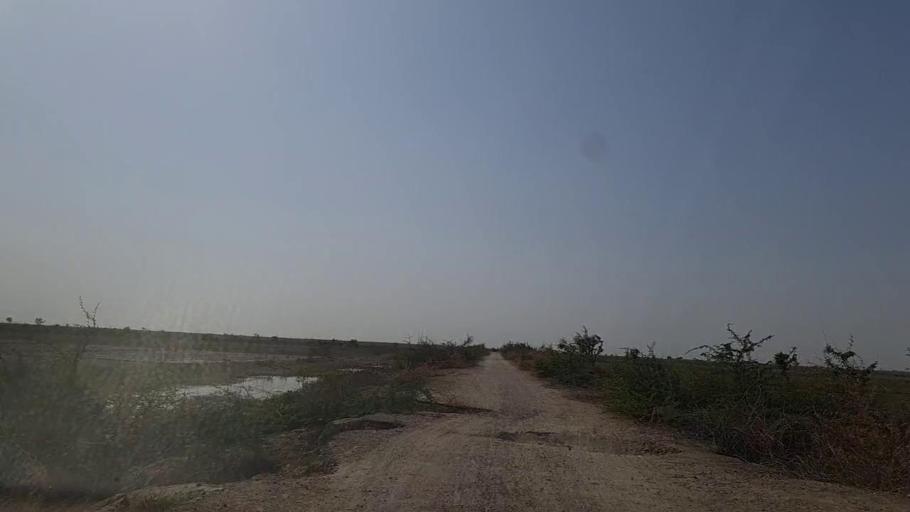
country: PK
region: Sindh
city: Naukot
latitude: 24.5950
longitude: 69.3115
